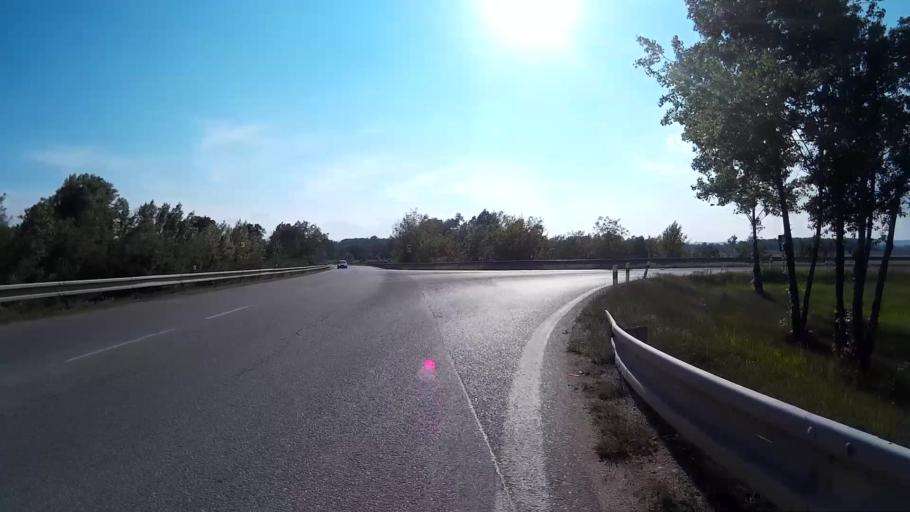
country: CZ
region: South Moravian
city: Pohorelice
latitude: 48.9949
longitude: 16.5471
